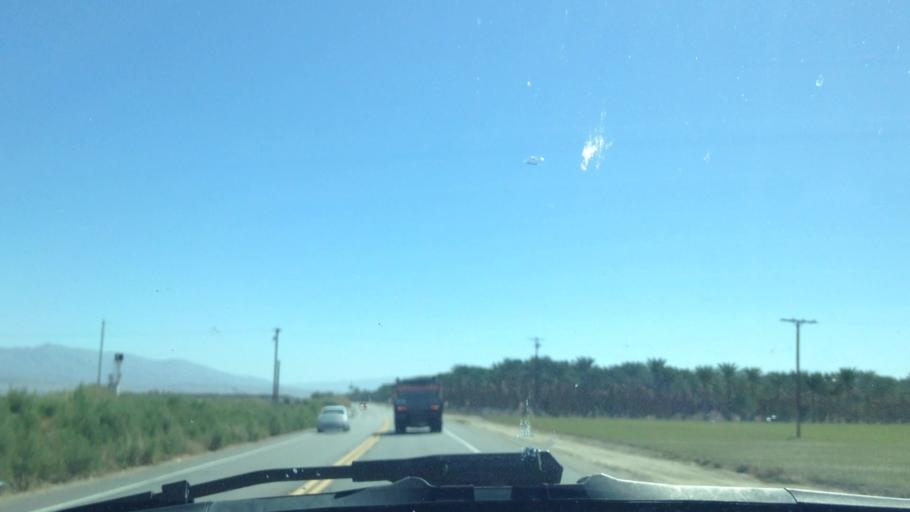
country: US
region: California
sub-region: Riverside County
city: Mecca
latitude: 33.5370
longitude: -116.0195
